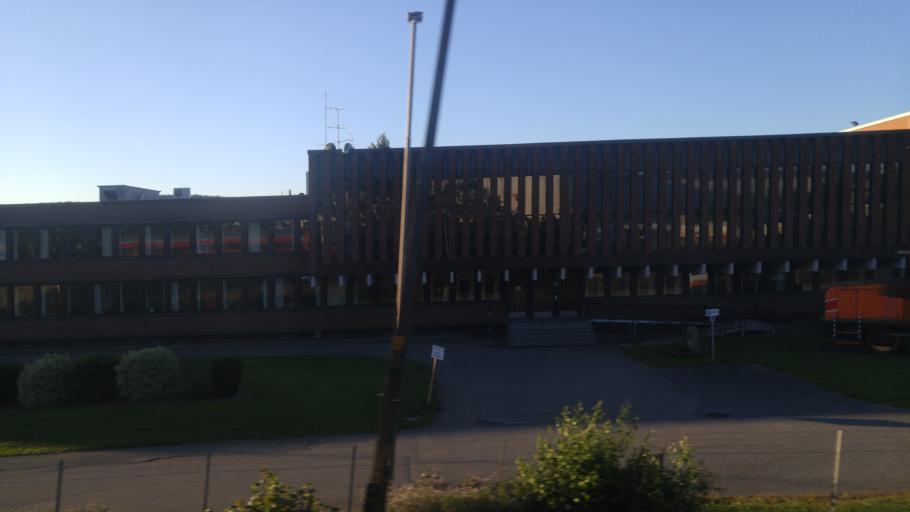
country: NO
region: Akershus
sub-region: Lorenskog
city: Kjenn
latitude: 59.9432
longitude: 10.8690
